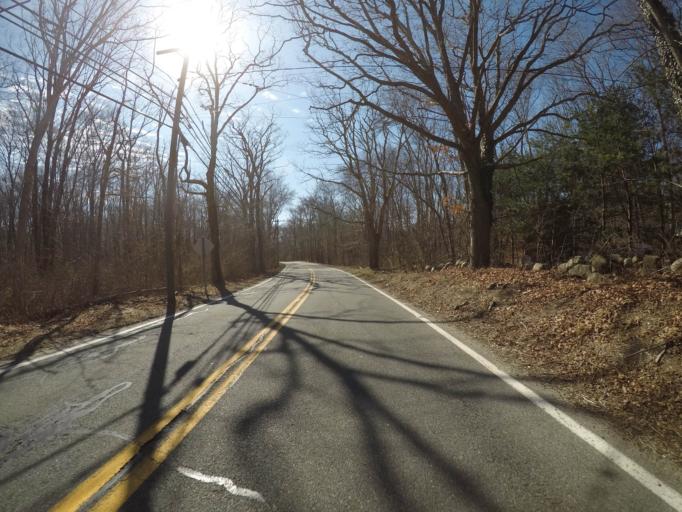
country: US
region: Massachusetts
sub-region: Norfolk County
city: Stoughton
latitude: 42.0822
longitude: -71.1394
